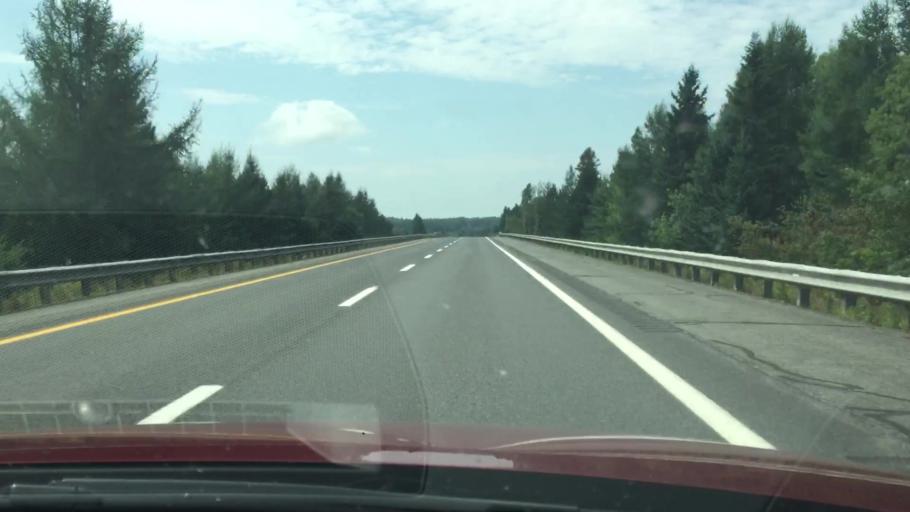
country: US
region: Maine
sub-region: Aroostook County
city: Hodgdon
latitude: 46.1137
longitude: -68.1469
